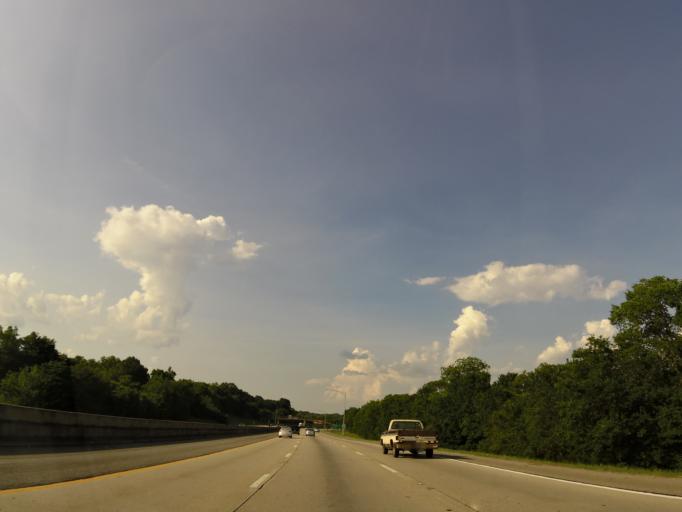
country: US
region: Alabama
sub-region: Jefferson County
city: Irondale
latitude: 33.5536
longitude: -86.7427
